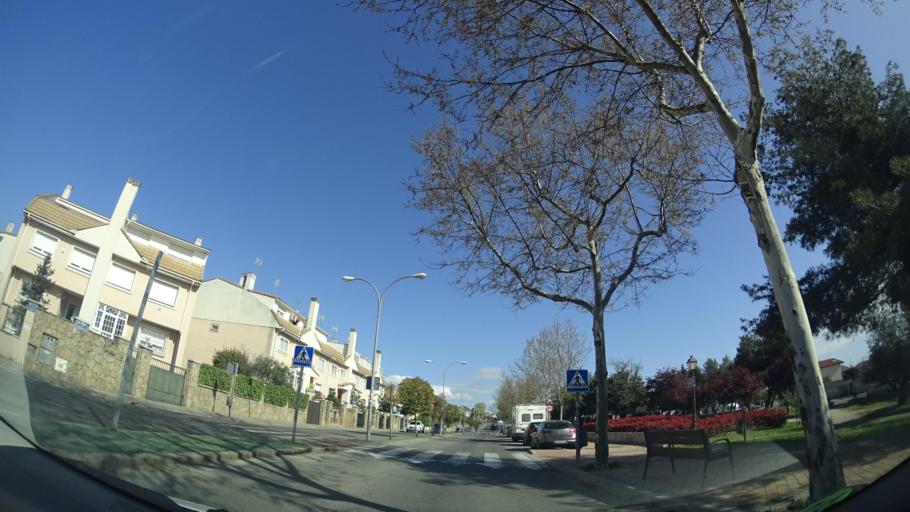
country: ES
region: Madrid
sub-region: Provincia de Madrid
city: Colmenar Viejo
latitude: 40.6566
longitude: -3.7759
